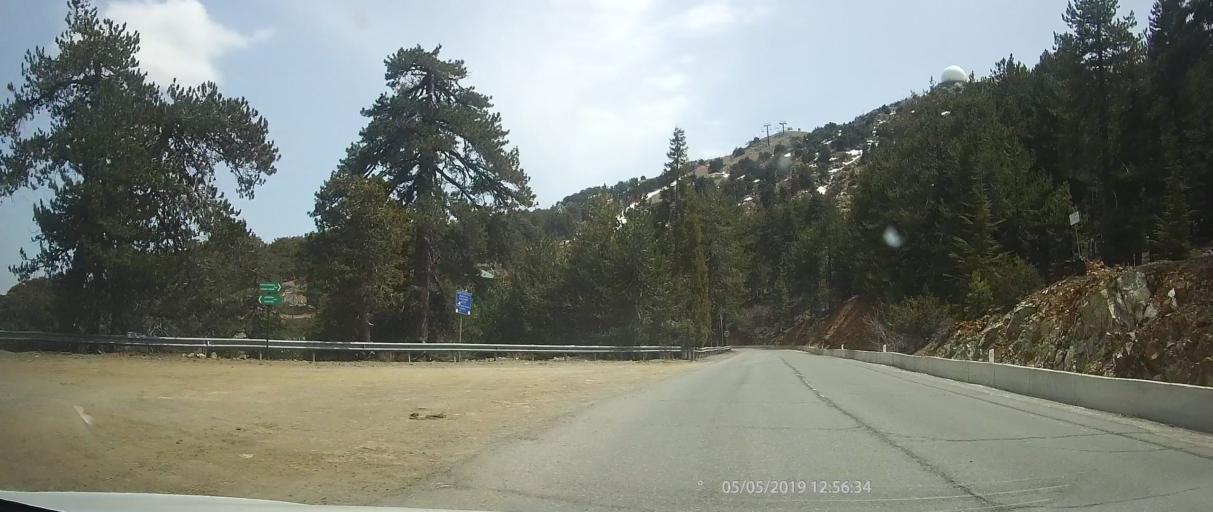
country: CY
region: Lefkosia
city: Kakopetria
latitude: 34.9409
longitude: 32.8645
